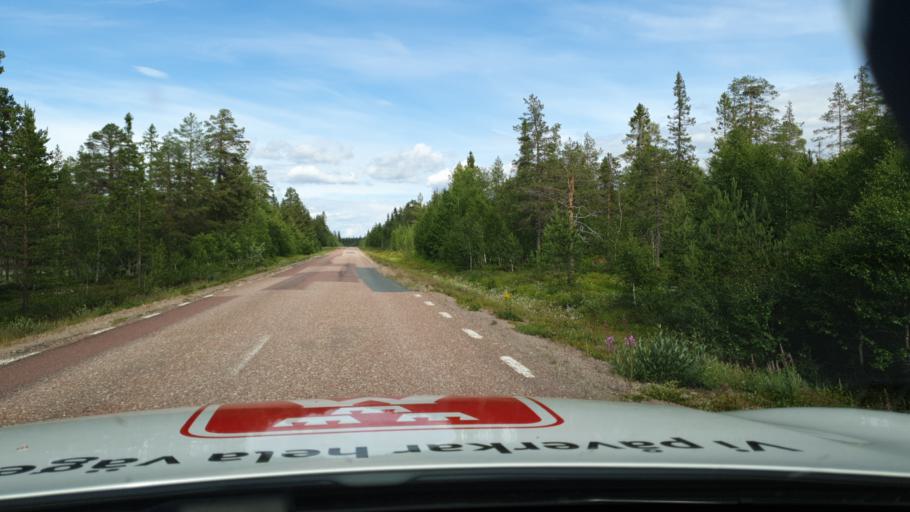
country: SE
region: Dalarna
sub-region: Alvdalens Kommun
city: AElvdalen
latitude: 61.7614
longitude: 13.4629
